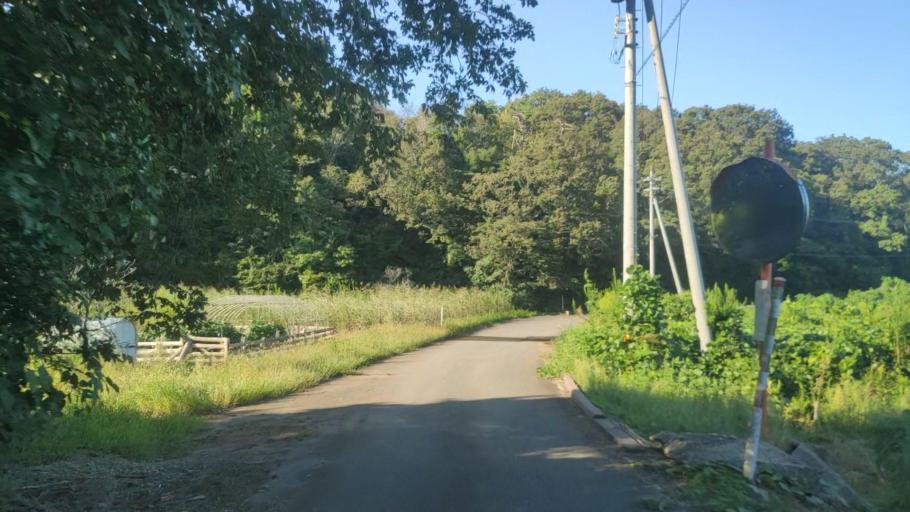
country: JP
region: Ishikawa
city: Nanao
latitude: 37.1236
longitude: 136.8947
